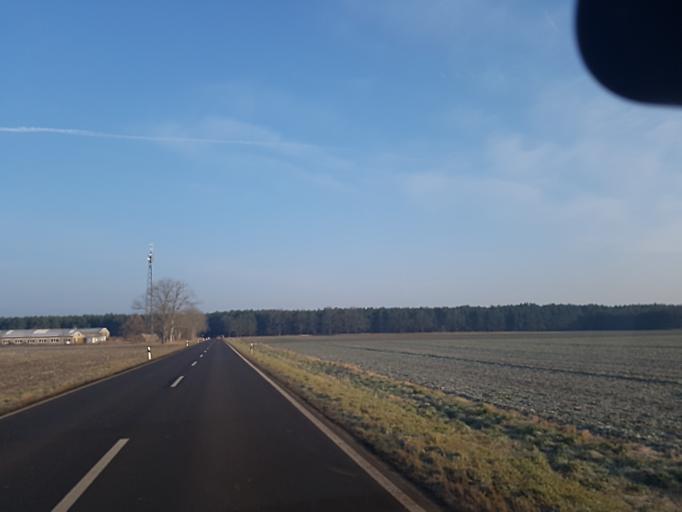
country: DE
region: Brandenburg
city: Bruck
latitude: 52.2081
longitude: 12.7512
